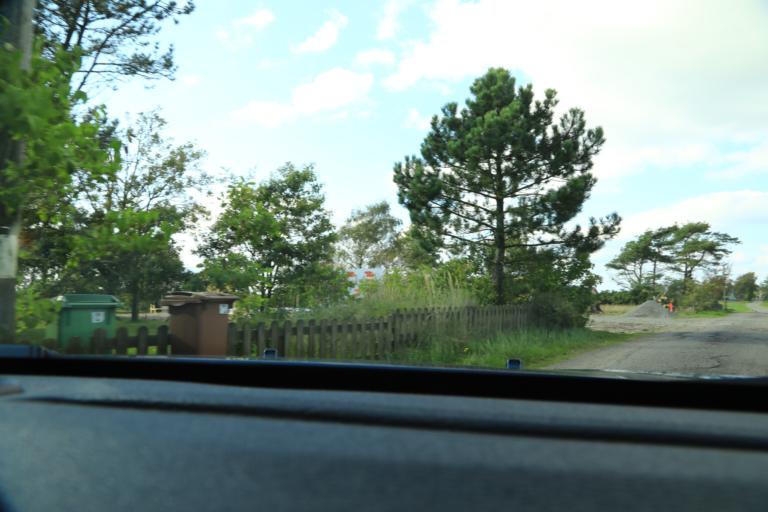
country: SE
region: Halland
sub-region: Varbergs Kommun
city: Tvaaker
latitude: 57.0113
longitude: 12.3508
